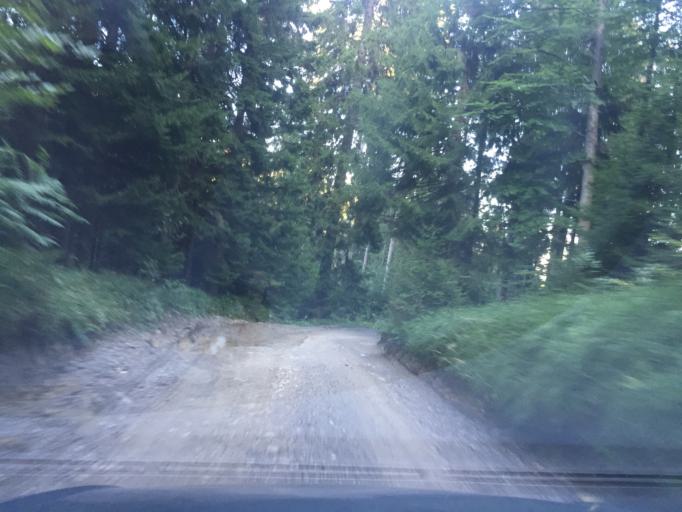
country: SI
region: Ravne na Koroskem
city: Kotlje
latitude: 46.4768
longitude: 14.9829
